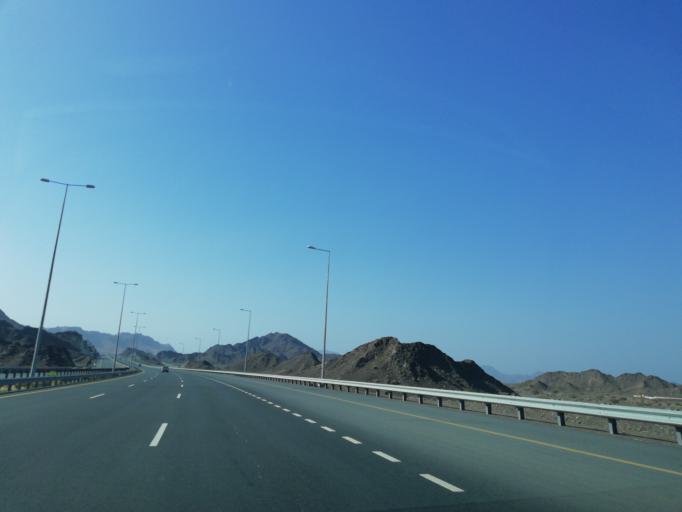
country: OM
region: Muhafazat ad Dakhiliyah
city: Sufalat Sama'il
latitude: 22.9788
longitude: 58.2339
